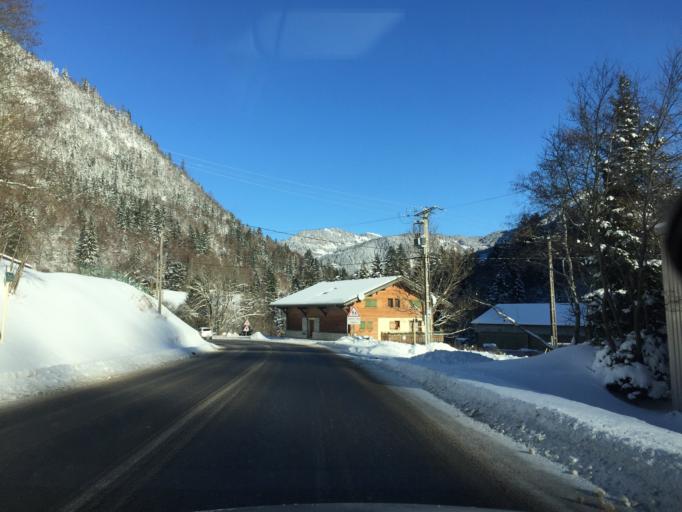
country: FR
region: Rhone-Alpes
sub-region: Departement de la Haute-Savoie
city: Abondance
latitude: 46.2992
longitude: 6.6743
